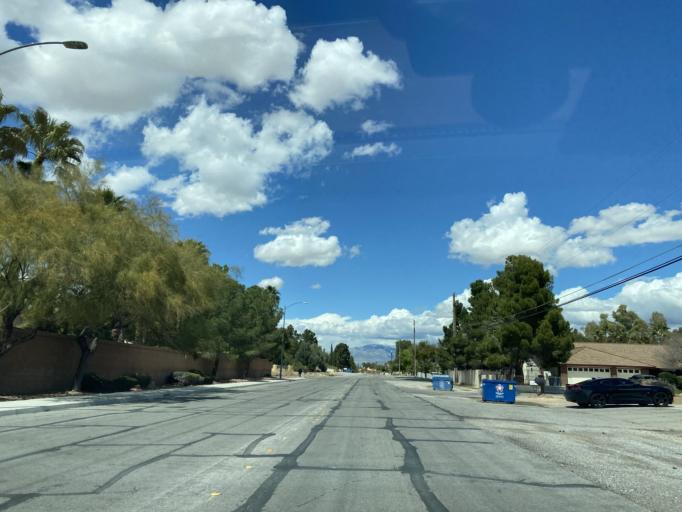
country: US
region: Nevada
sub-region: Clark County
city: Spring Valley
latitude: 36.2508
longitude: -115.2698
